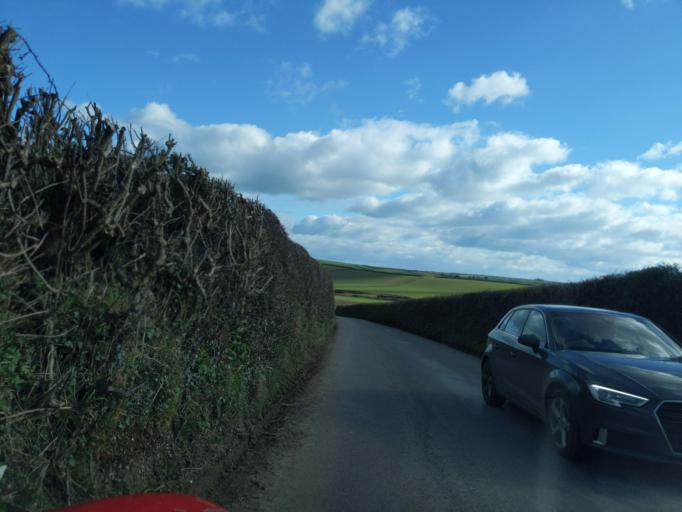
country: GB
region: England
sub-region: Devon
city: Salcombe
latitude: 50.2619
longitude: -3.7171
